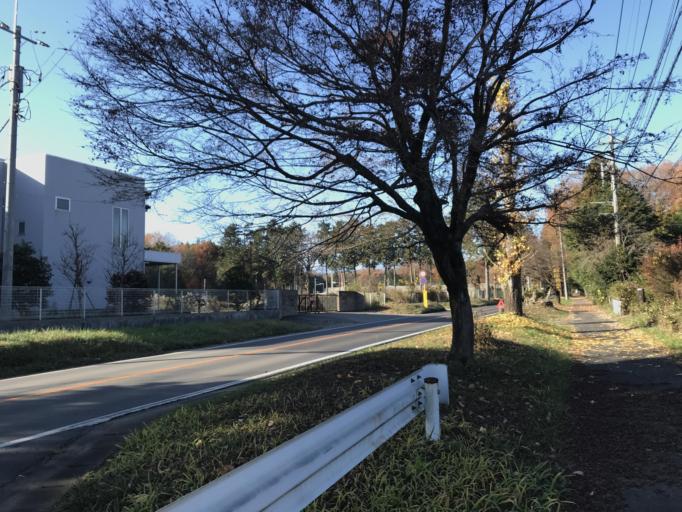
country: JP
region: Tochigi
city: Kanuma
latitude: 36.6109
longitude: 139.7398
